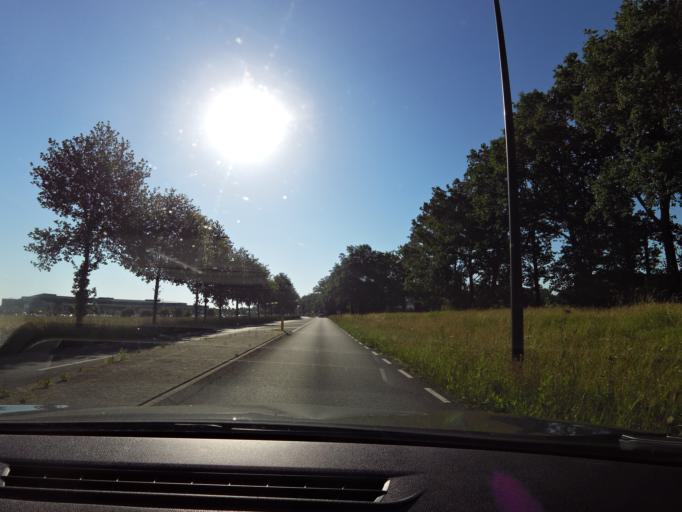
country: NL
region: Overijssel
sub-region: Gemeente Deventer
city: Schalkhaar
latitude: 52.2603
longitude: 6.1856
